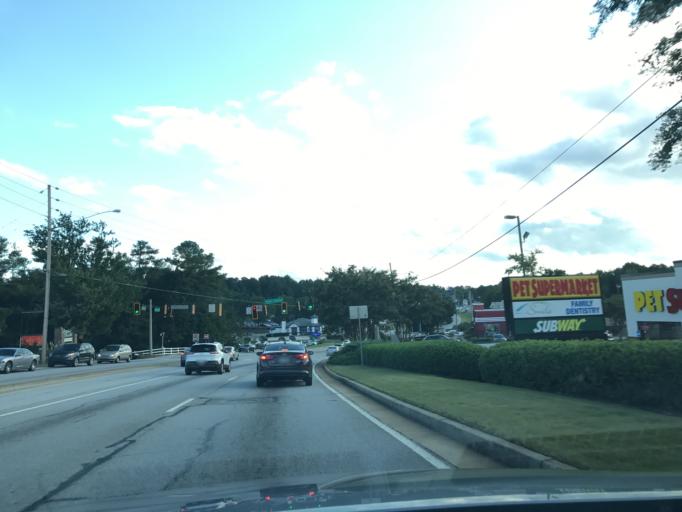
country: US
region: Georgia
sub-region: Douglas County
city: Douglasville
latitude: 33.7231
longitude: -84.7626
